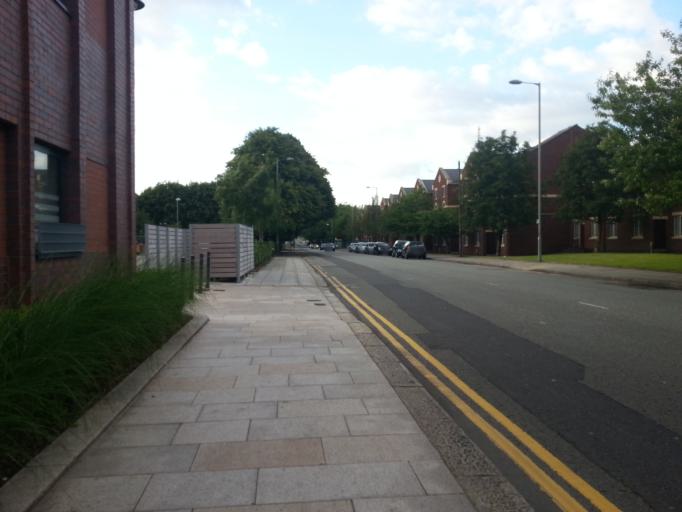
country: GB
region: England
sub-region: Liverpool
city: Liverpool
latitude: 53.4012
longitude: -2.9624
